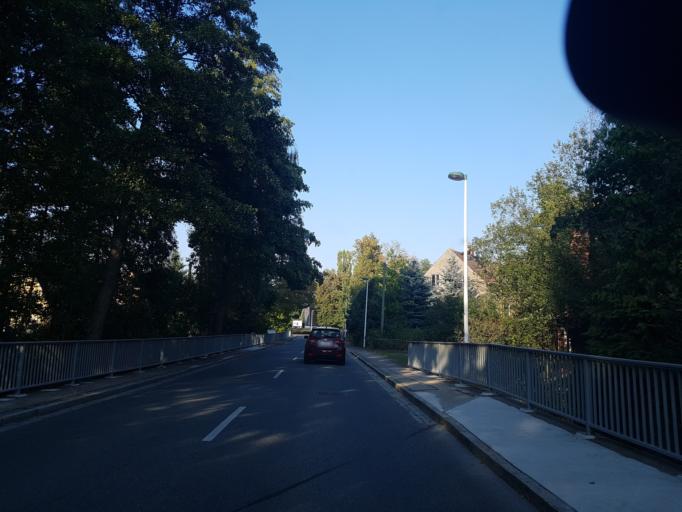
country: DE
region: Saxony
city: Strehla
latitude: 51.3118
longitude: 13.2173
